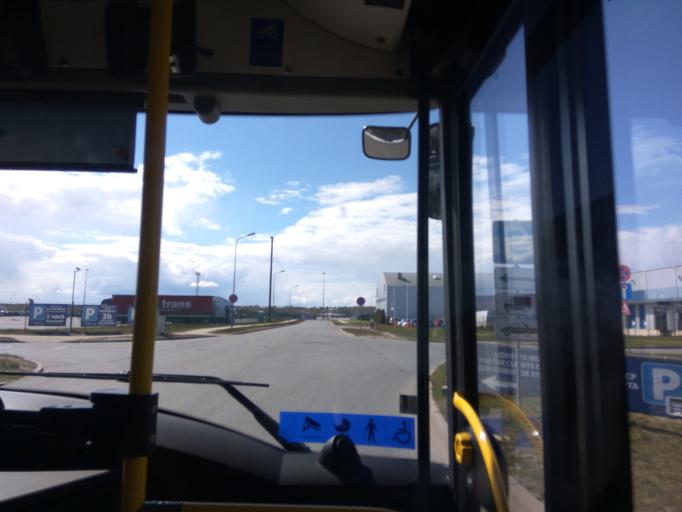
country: LV
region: Marupe
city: Marupe
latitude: 56.9277
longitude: 23.9868
